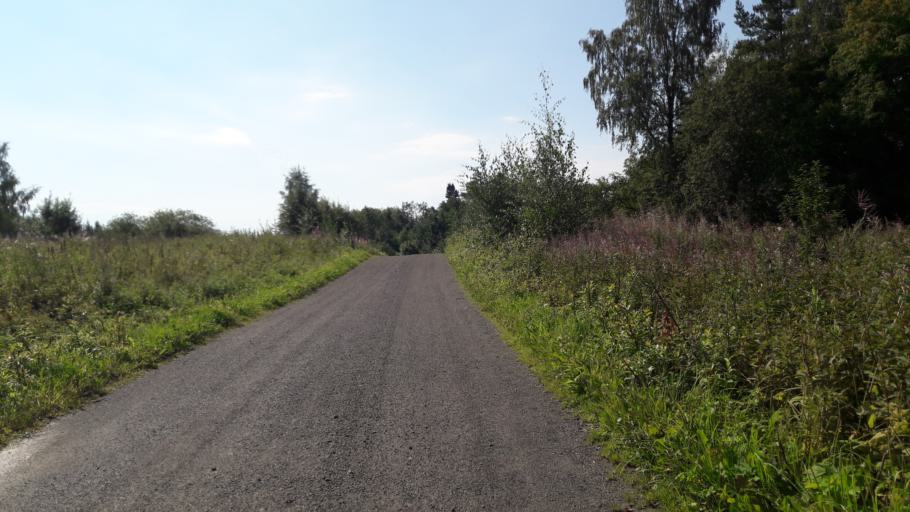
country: FI
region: North Karelia
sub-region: Joensuu
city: Joensuu
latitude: 62.5301
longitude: 29.8351
